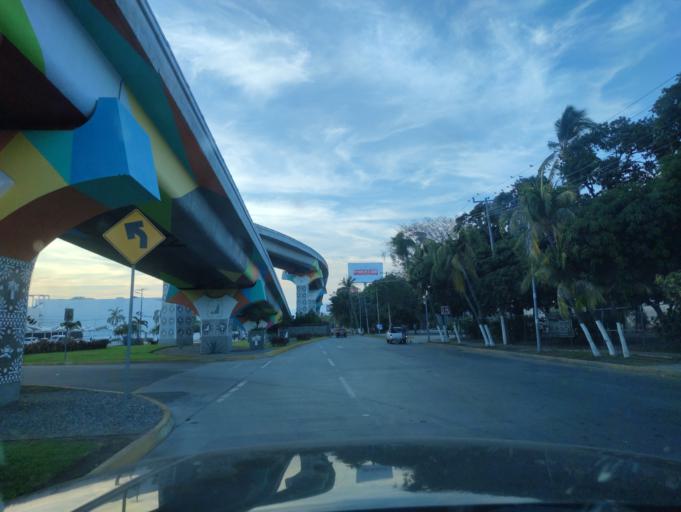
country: MX
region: Guerrero
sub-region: Acapulco de Juarez
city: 10 de Abril
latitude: 16.7716
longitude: -99.7727
